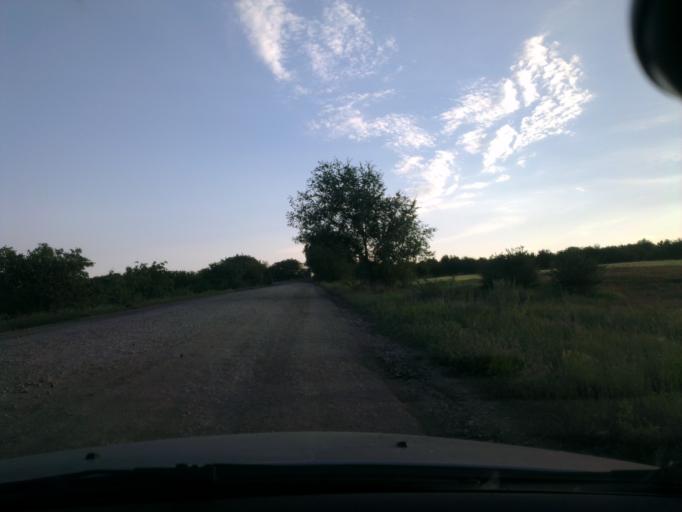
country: MD
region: Cantemir
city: Visniovca
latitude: 46.3477
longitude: 28.4051
